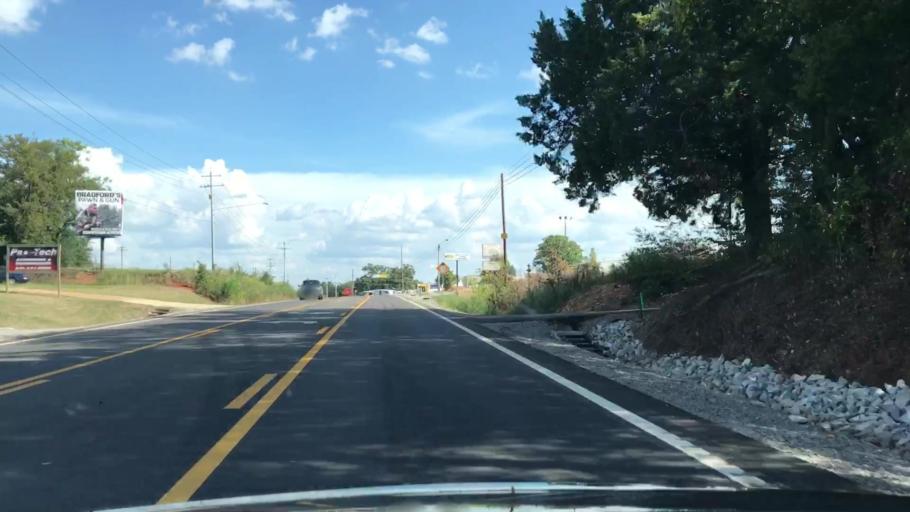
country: US
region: Alabama
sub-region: Limestone County
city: Ardmore
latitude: 34.9983
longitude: -86.8620
